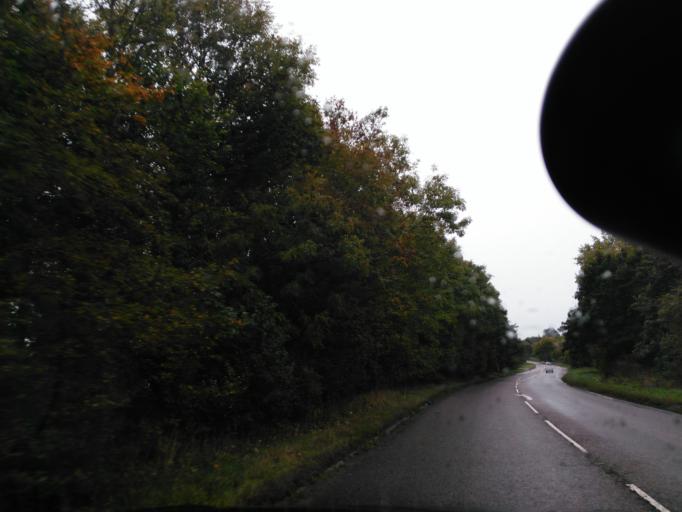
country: GB
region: England
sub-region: Wiltshire
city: Lacock
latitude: 51.4303
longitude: -2.1301
